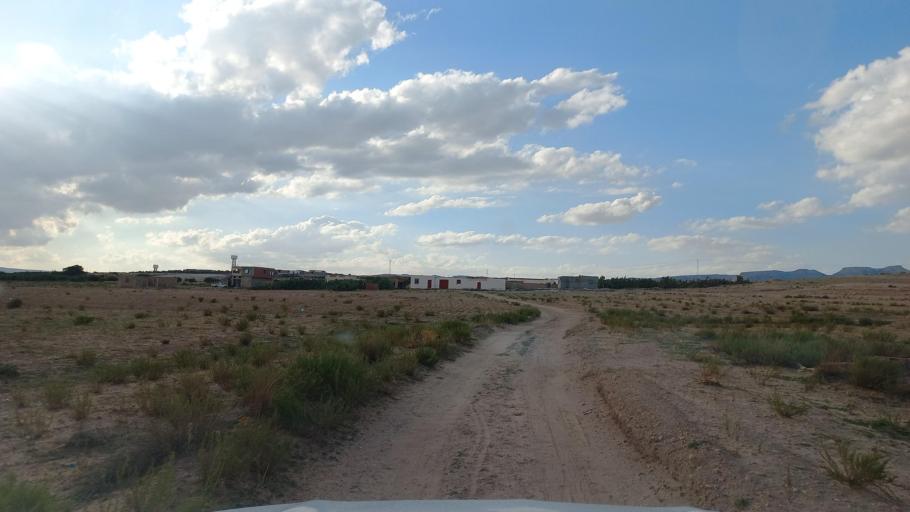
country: TN
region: Al Qasrayn
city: Sbiba
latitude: 35.3886
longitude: 9.0538
